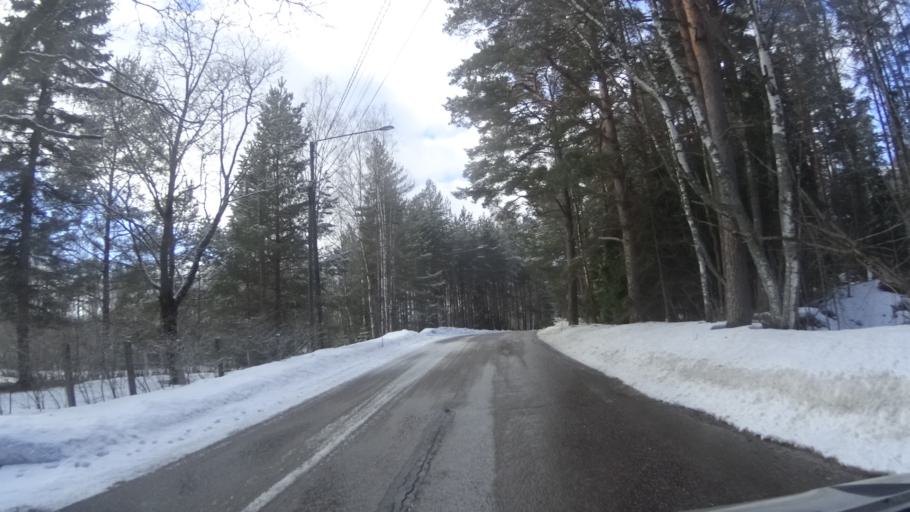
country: FI
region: Uusimaa
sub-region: Helsinki
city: Vantaa
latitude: 60.2530
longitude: 25.1671
